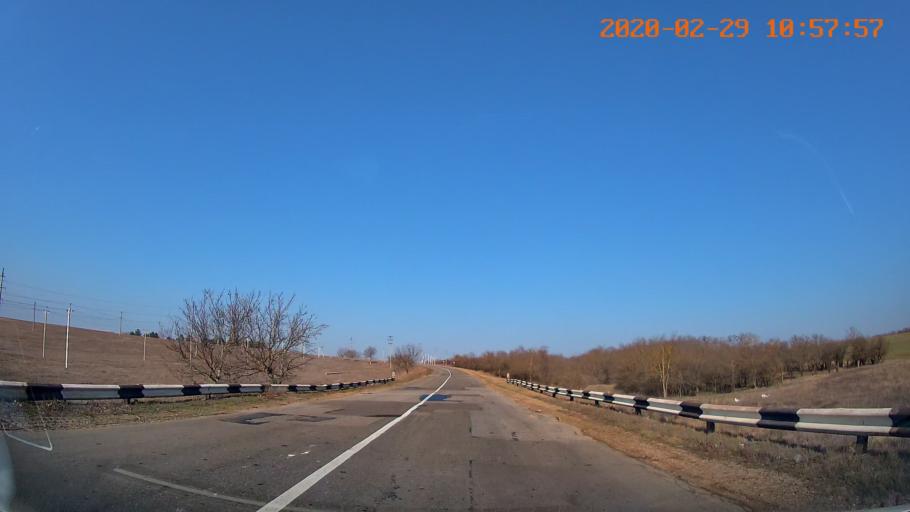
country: MD
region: Telenesti
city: Grigoriopol
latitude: 47.1653
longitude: 29.3185
